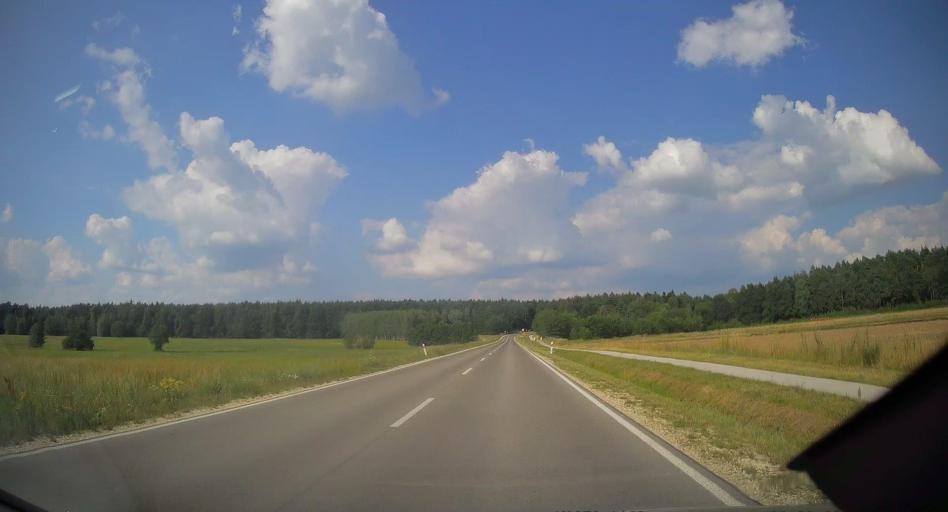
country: PL
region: Swietokrzyskie
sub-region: Powiat kielecki
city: Lopuszno
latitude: 51.0024
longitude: 20.2717
